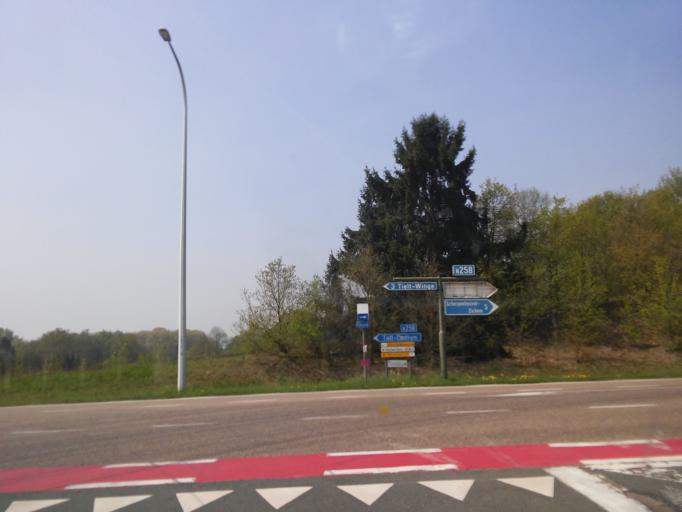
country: BE
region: Flanders
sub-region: Provincie Vlaams-Brabant
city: Bekkevoort
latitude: 50.9556
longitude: 4.9305
